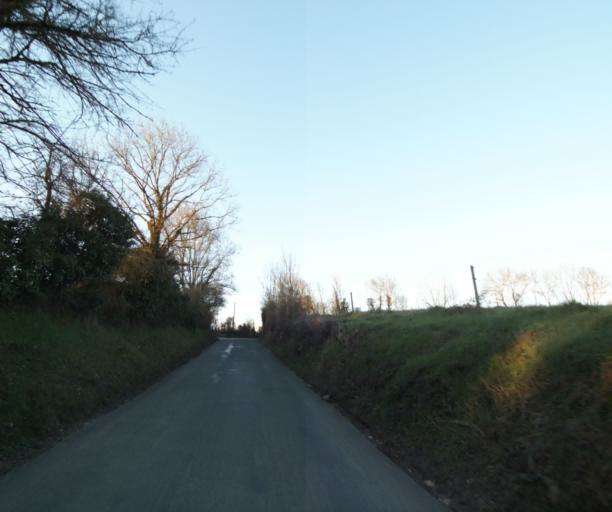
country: FR
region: Poitou-Charentes
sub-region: Departement des Deux-Sevres
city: Niort
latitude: 46.3600
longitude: -0.4522
